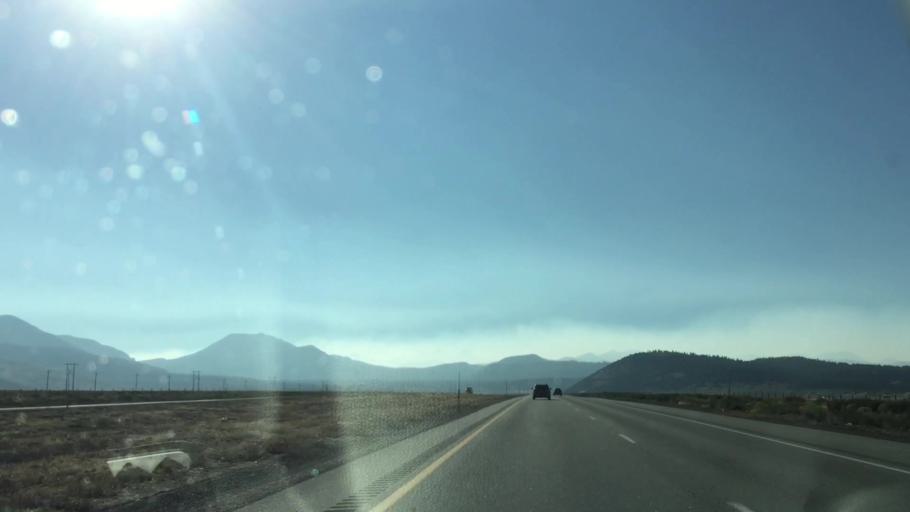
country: US
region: California
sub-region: Mono County
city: Mammoth Lakes
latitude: 37.6247
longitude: -118.8456
